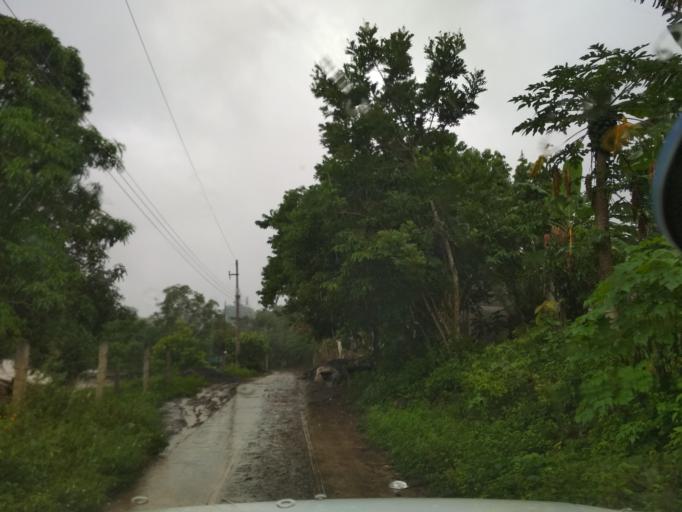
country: MX
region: Veracruz
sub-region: San Andres Tuxtla
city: Soyata
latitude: 18.4089
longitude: -95.2993
